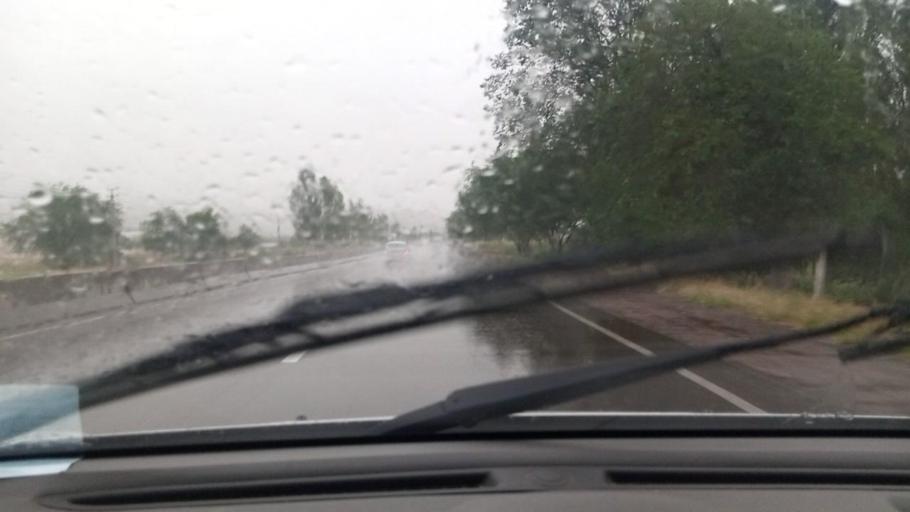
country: UZ
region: Toshkent
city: Ohangaron
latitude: 40.9230
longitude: 69.8414
